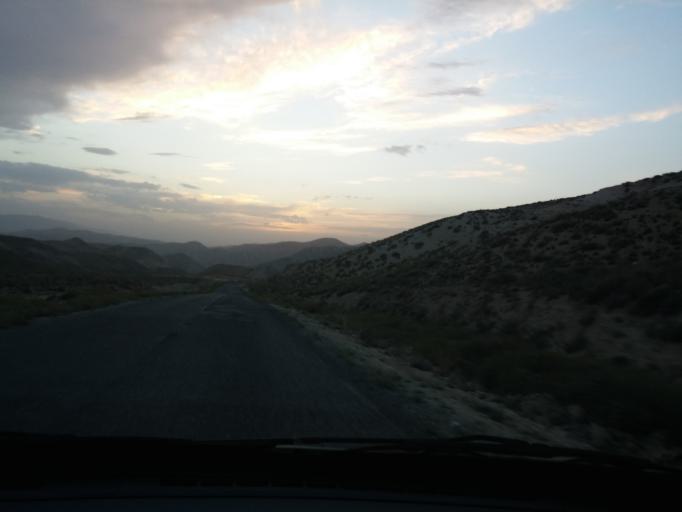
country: IR
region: Tehran
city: Damavand
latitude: 35.5397
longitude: 52.2936
